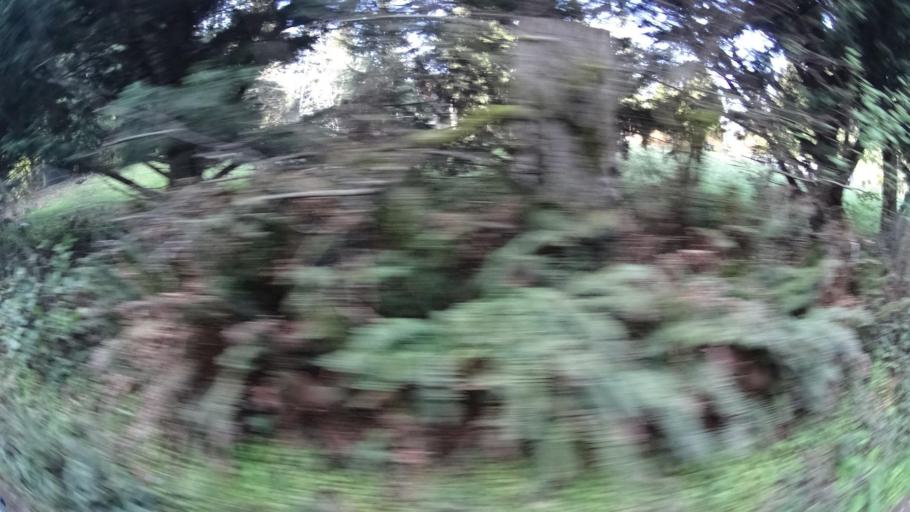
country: US
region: California
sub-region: Humboldt County
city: Bayside
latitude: 40.7540
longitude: -123.9863
